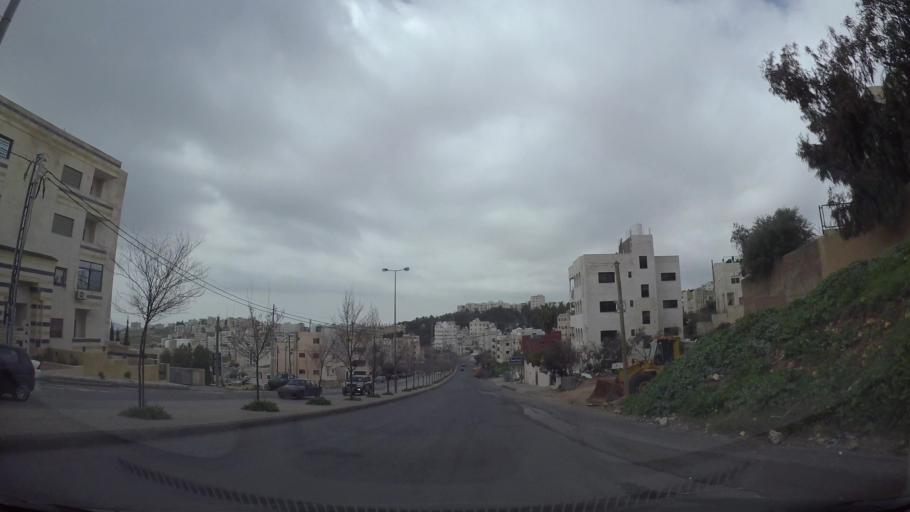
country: JO
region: Amman
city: Wadi as Sir
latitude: 31.9462
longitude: 35.8265
